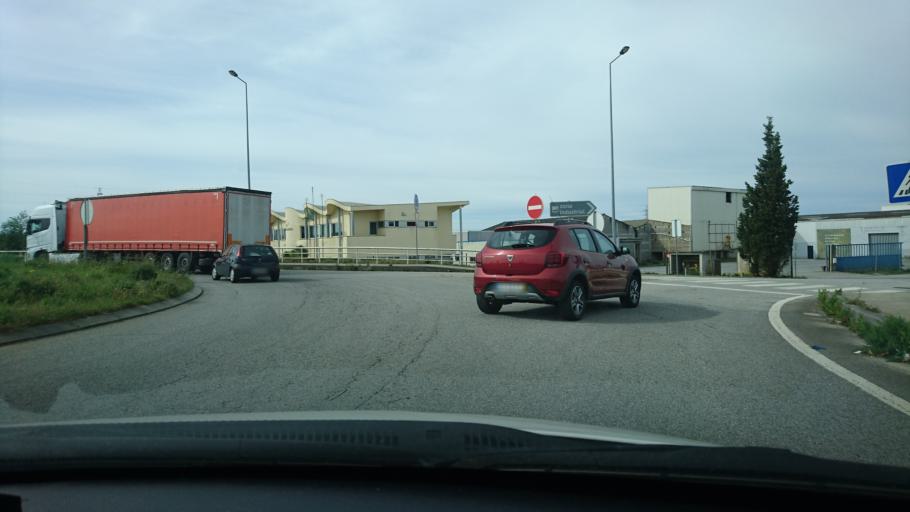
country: PT
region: Aveiro
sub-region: Albergaria-A-Velha
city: Albergaria-a-Velha
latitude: 40.7127
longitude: -8.4831
